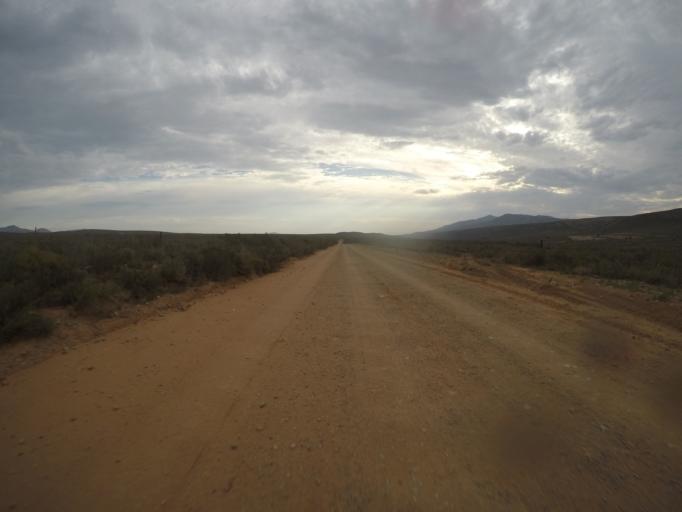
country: ZA
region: Eastern Cape
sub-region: Cacadu District Municipality
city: Willowmore
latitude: -33.4921
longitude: 23.5853
